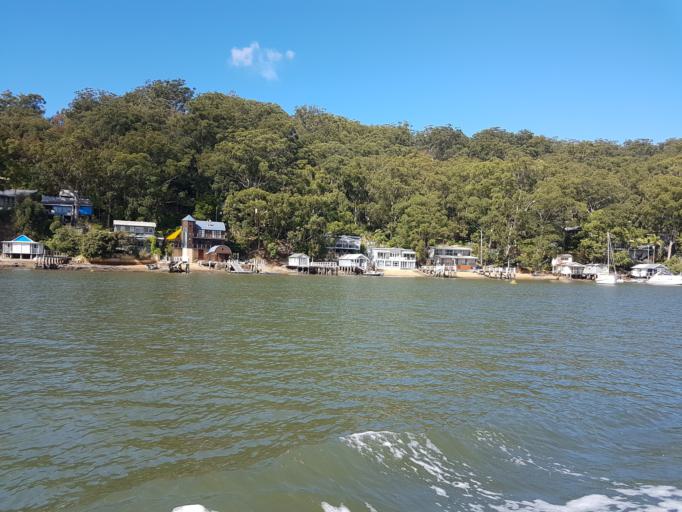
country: AU
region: New South Wales
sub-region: Gosford Shire
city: Umina
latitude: -33.5378
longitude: 151.2348
